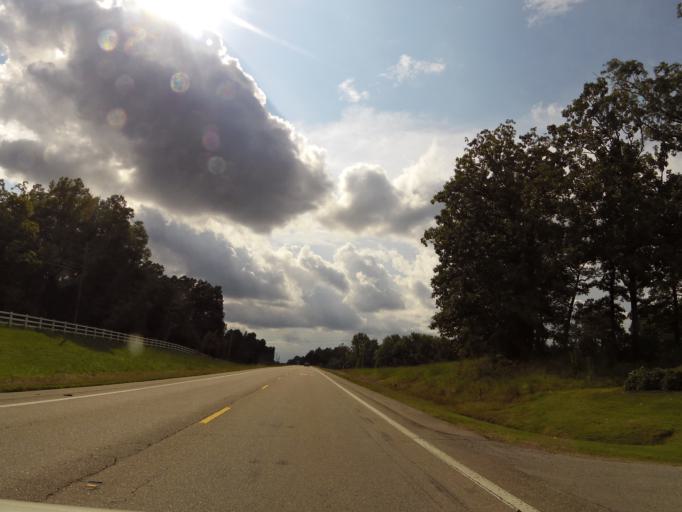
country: US
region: Mississippi
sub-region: Alcorn County
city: Corinth
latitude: 34.9819
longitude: -88.4858
